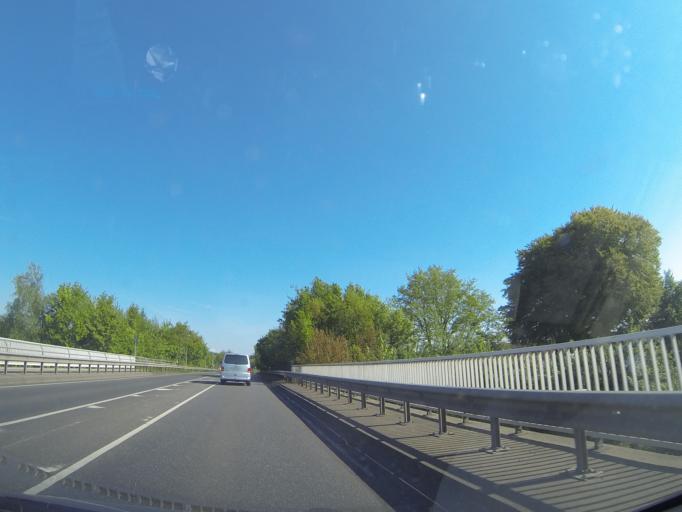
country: DE
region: Schleswig-Holstein
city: Halstenbek
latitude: 53.6398
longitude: 9.8388
